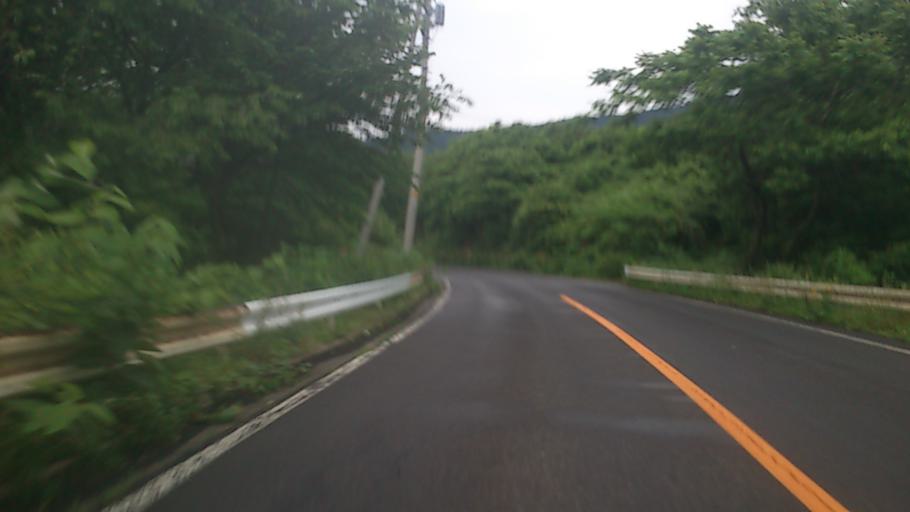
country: JP
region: Akita
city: Noshiromachi
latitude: 40.3921
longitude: 139.9821
